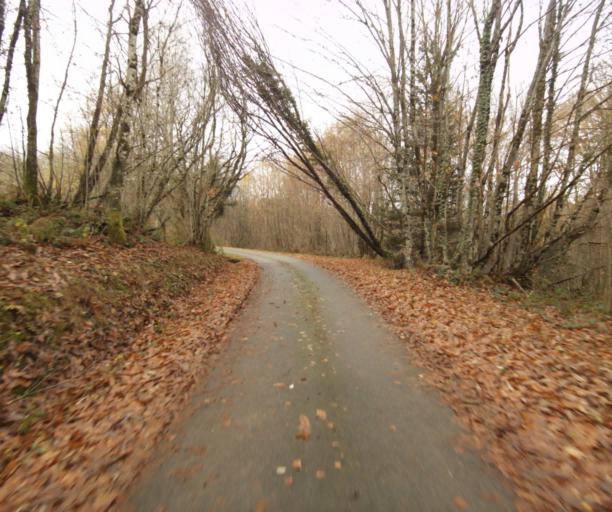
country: FR
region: Limousin
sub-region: Departement de la Correze
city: Sainte-Fortunade
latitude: 45.1772
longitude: 1.7740
